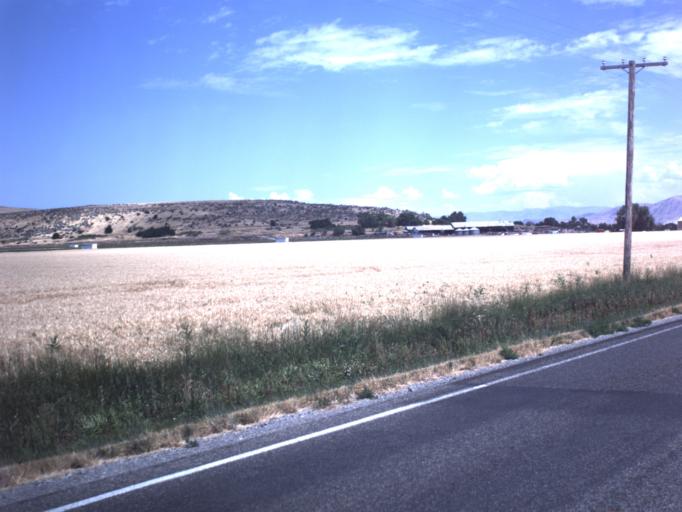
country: US
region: Utah
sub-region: Box Elder County
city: Tremonton
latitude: 41.7101
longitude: -112.2354
